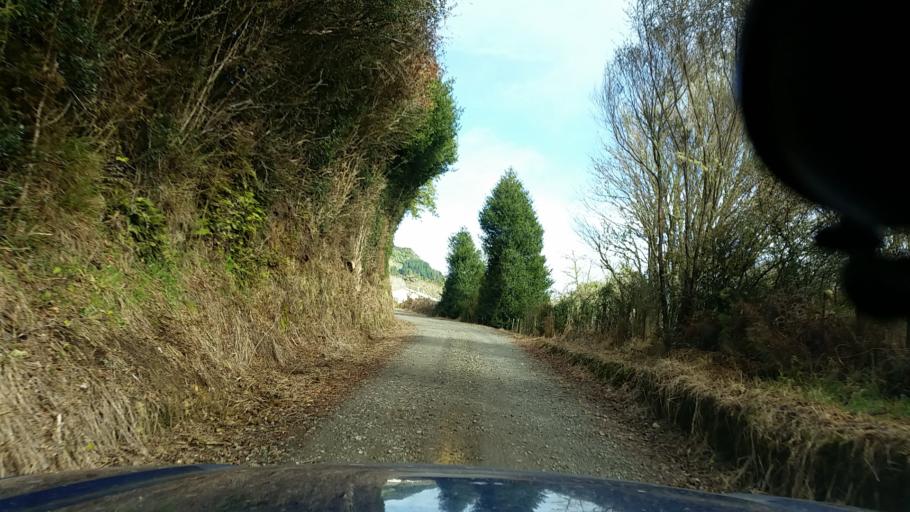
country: NZ
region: Taranaki
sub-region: New Plymouth District
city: Waitara
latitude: -39.0322
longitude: 174.8013
